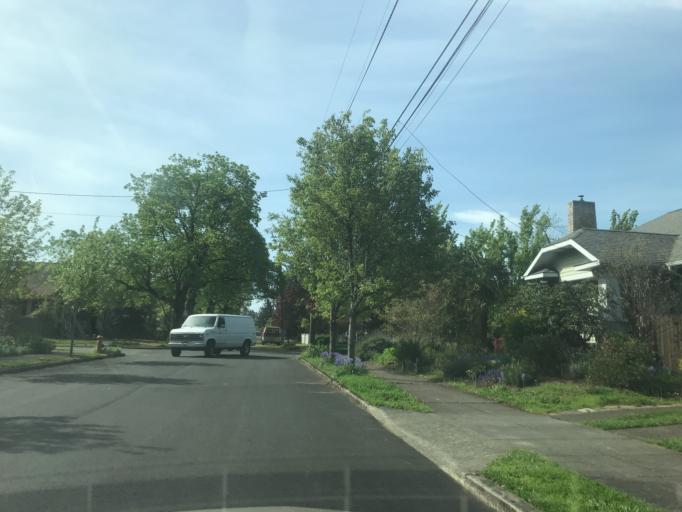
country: US
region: Oregon
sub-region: Multnomah County
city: Lents
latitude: 45.4889
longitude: -122.5904
